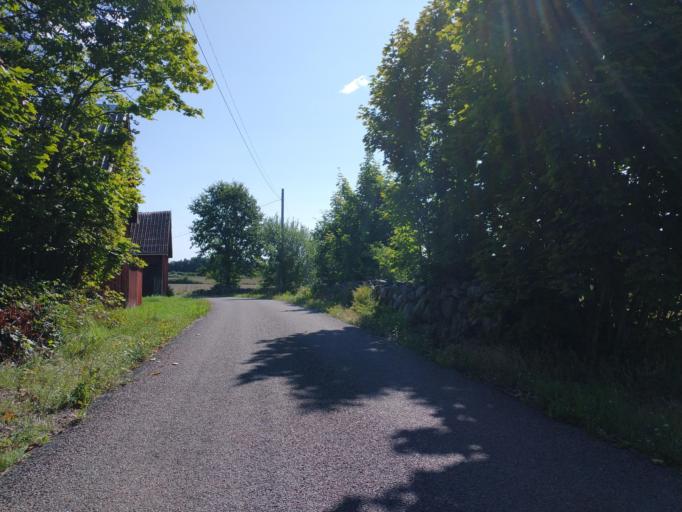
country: SE
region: Kalmar
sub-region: Kalmar Kommun
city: Lindsdal
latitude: 56.7949
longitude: 16.2738
